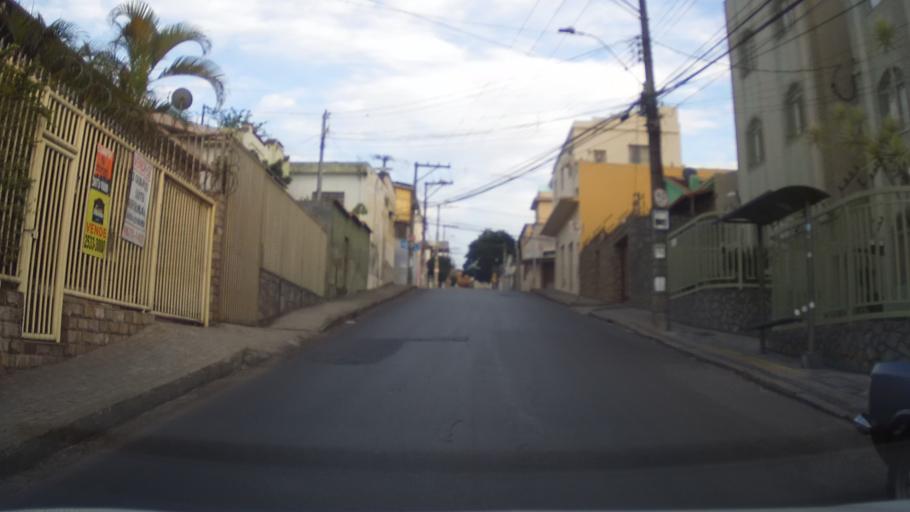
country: BR
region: Minas Gerais
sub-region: Belo Horizonte
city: Belo Horizonte
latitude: -19.9155
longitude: -43.9651
